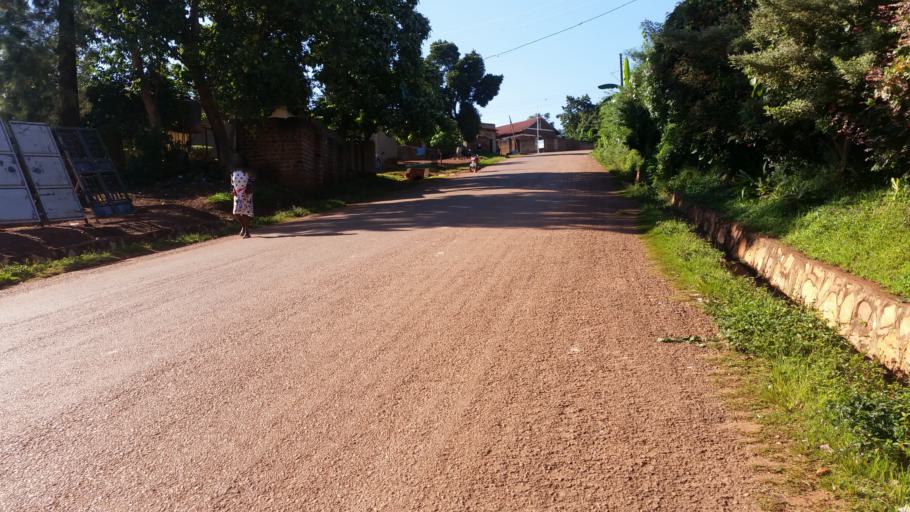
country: UG
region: Central Region
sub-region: Wakiso District
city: Kireka
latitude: 0.3384
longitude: 32.6462
